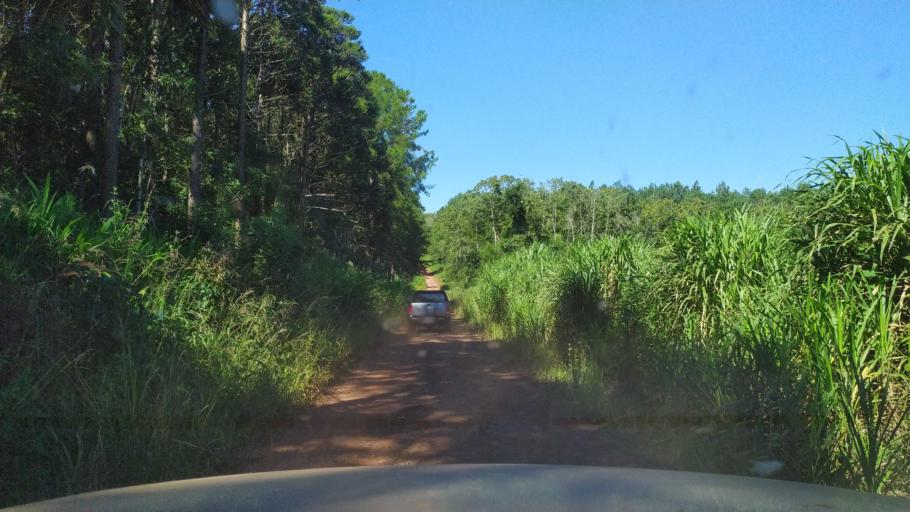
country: AR
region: Misiones
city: Caraguatay
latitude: -26.6739
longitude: -54.6987
